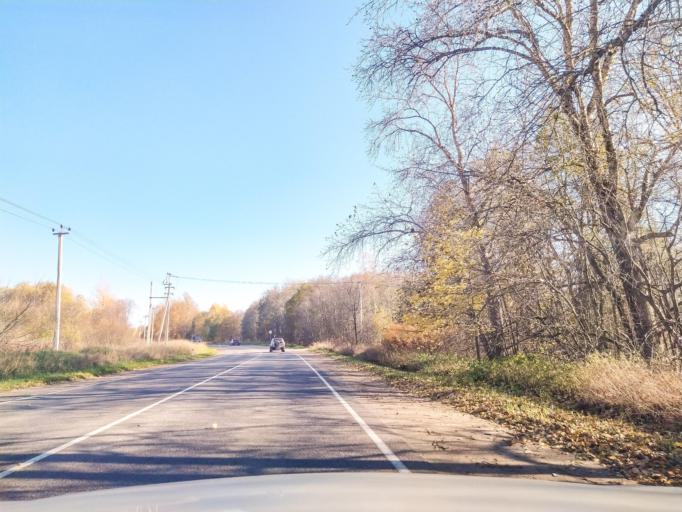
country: RU
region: Leningrad
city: Rozhdestveno
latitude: 59.3458
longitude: 29.9778
